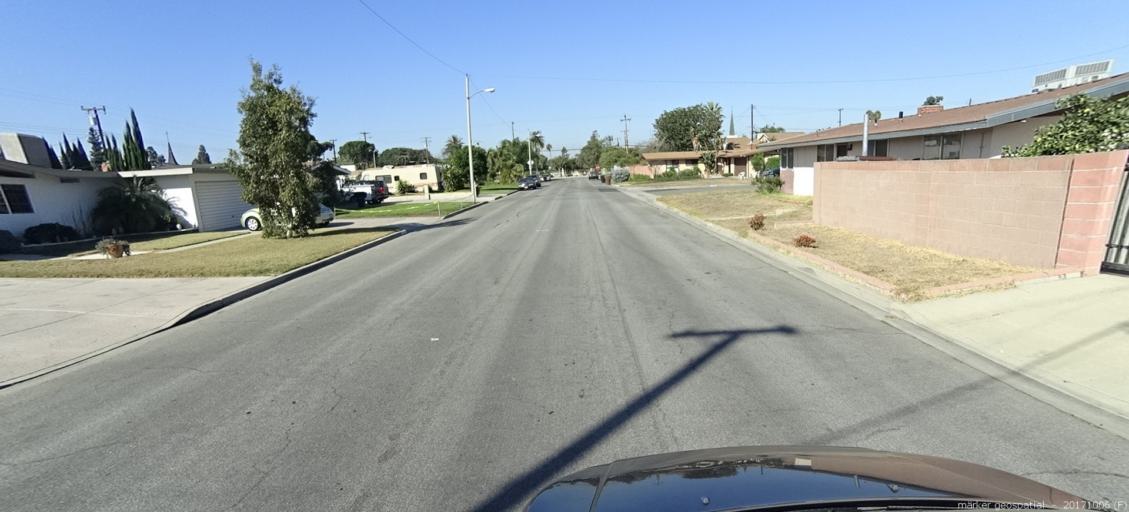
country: US
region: California
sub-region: Orange County
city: Stanton
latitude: 33.7847
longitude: -117.9739
